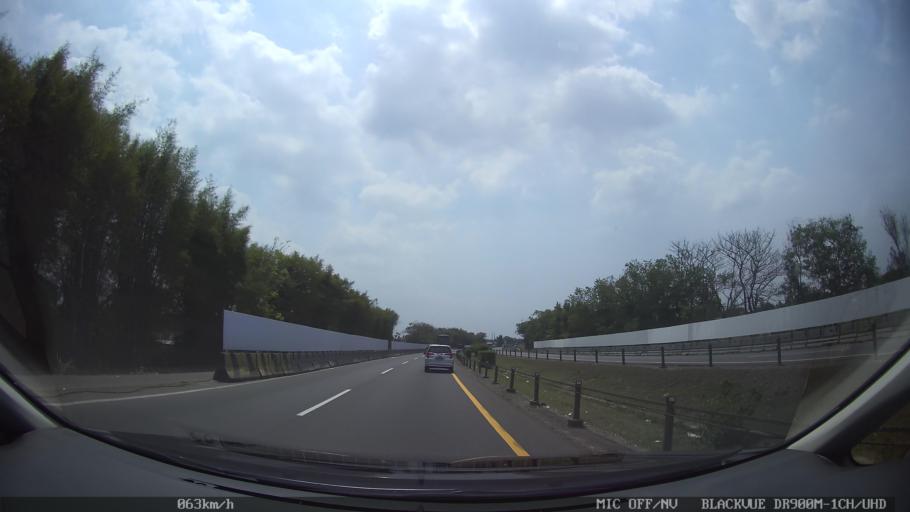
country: ID
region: Banten
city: Serang
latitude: -6.1281
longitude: 106.1944
